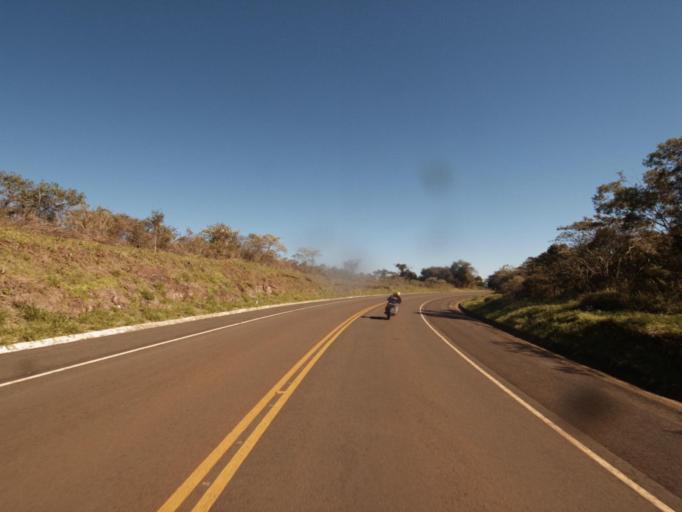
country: AR
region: Misiones
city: Bernardo de Irigoyen
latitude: -26.6131
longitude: -53.6959
